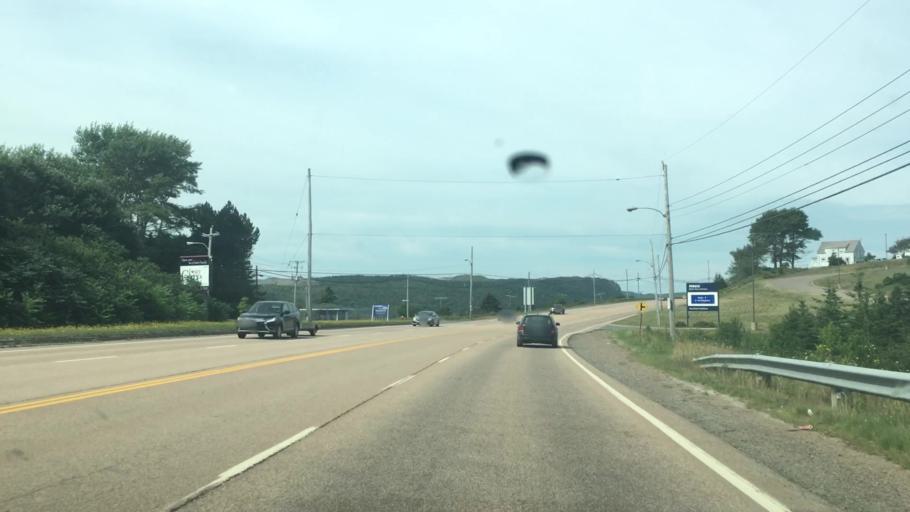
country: CA
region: Nova Scotia
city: Port Hawkesbury
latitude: 45.6254
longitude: -61.3684
